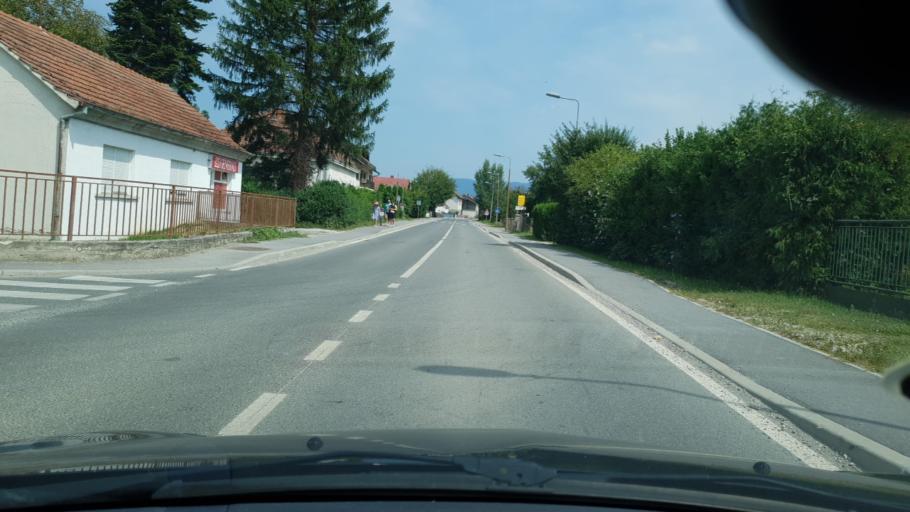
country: HR
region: Krapinsko-Zagorska
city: Marija Bistrica
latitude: 46.0467
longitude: 16.0846
